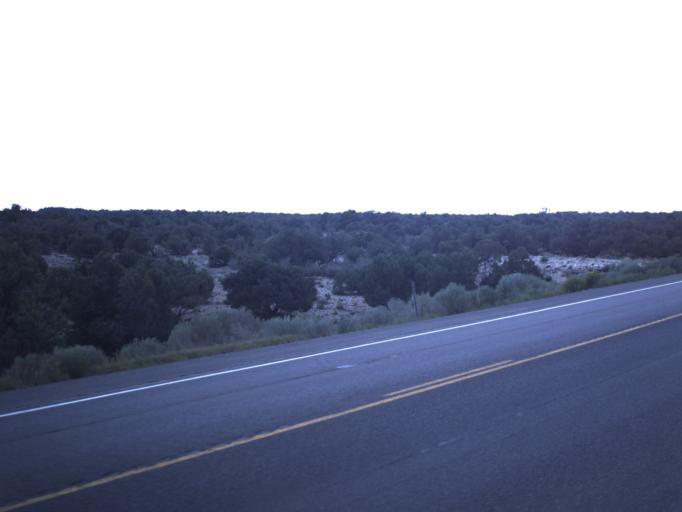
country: US
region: Utah
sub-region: Duchesne County
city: Duchesne
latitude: 40.1642
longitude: -110.4535
